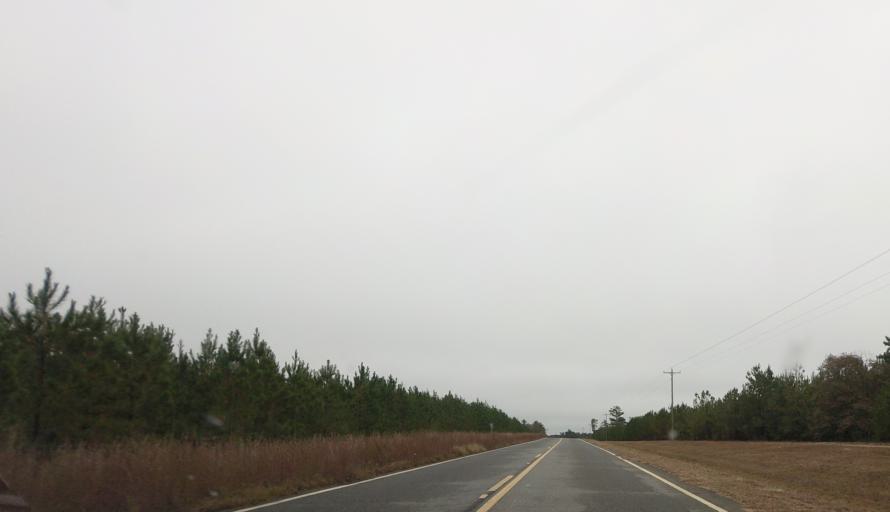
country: US
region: Georgia
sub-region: Taylor County
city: Butler
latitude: 32.4331
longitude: -84.3139
